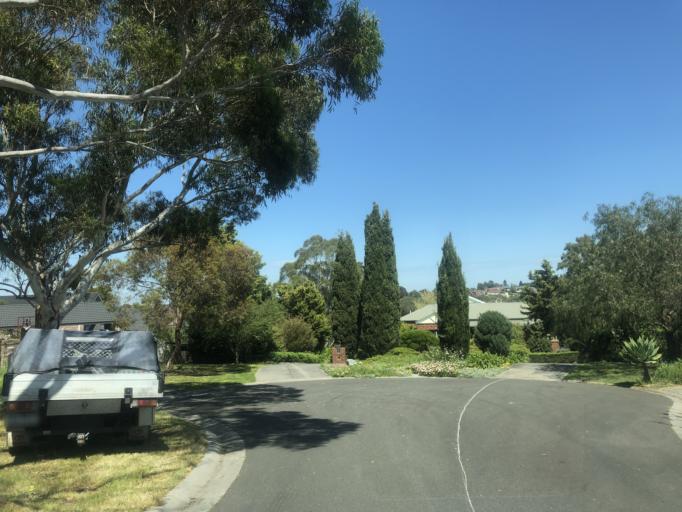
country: AU
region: Victoria
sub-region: Casey
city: Narre Warren North
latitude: -37.9849
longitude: 145.2874
